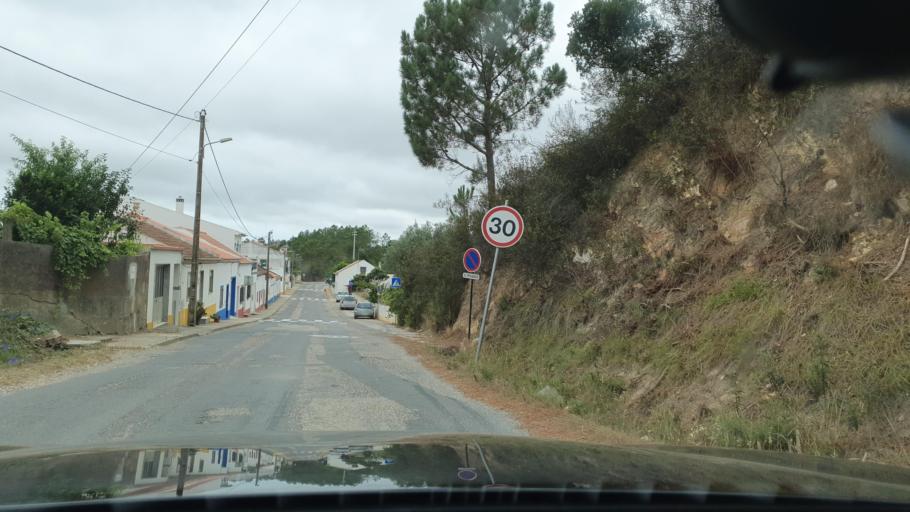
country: PT
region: Beja
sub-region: Odemira
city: Sao Teotonio
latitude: 37.5058
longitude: -8.6934
